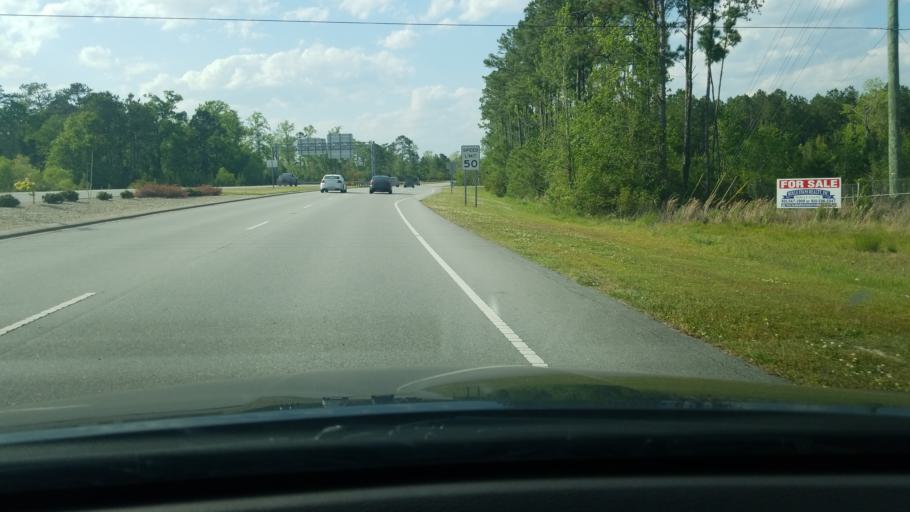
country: US
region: North Carolina
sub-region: Onslow County
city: Pumpkin Center
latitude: 34.7755
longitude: -77.3998
